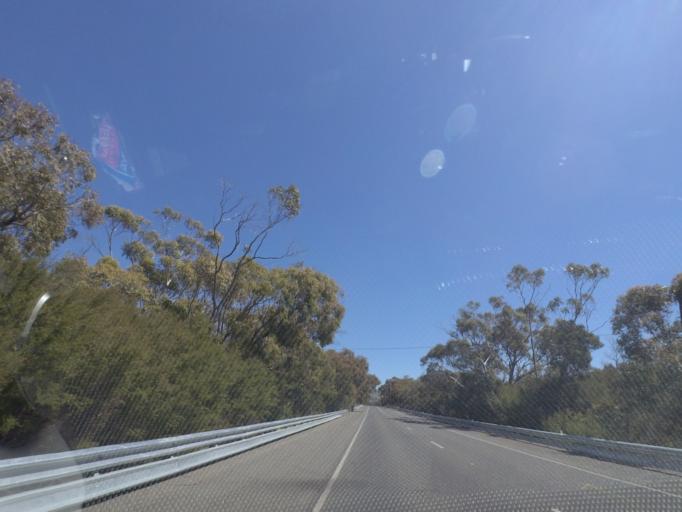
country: AU
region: Victoria
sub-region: Hume
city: Sunbury
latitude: -37.3027
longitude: 144.8307
